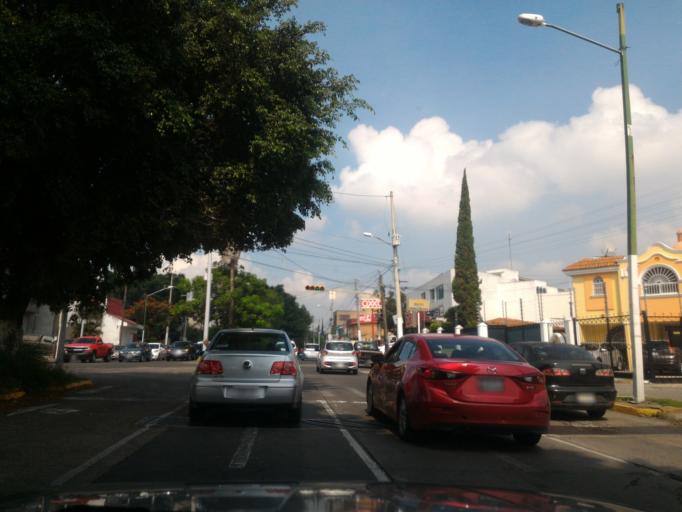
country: MX
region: Jalisco
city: Guadalajara
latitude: 20.6330
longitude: -103.4105
